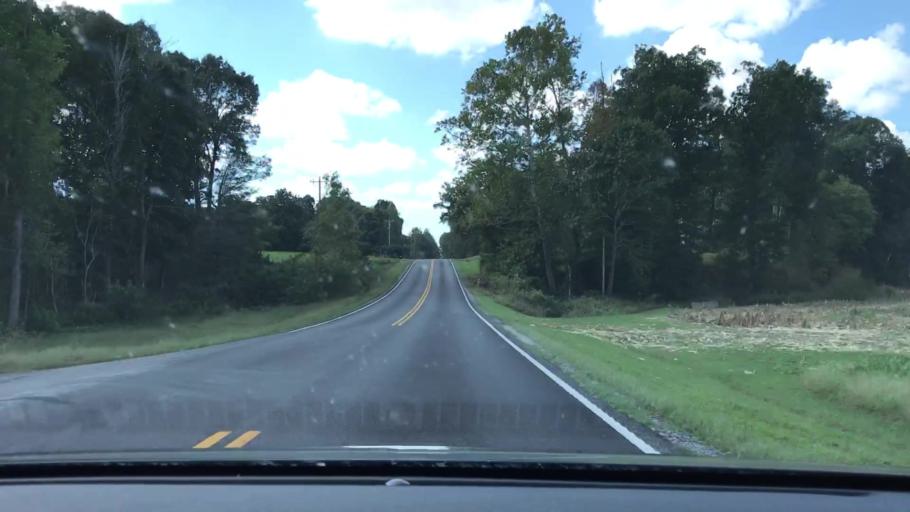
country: US
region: Kentucky
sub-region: McCracken County
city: Reidland
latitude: 36.8769
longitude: -88.5639
